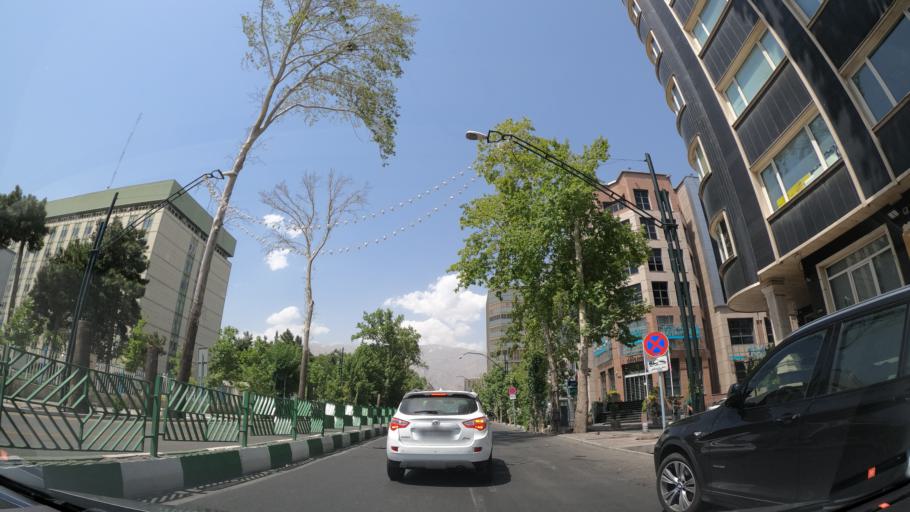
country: IR
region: Tehran
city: Tajrish
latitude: 35.7815
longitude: 51.4142
